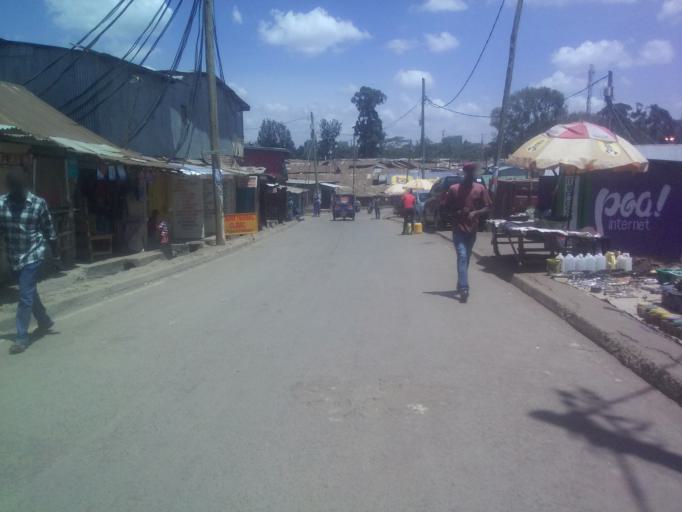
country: KE
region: Nairobi Area
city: Nairobi
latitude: -1.3078
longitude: 36.7862
